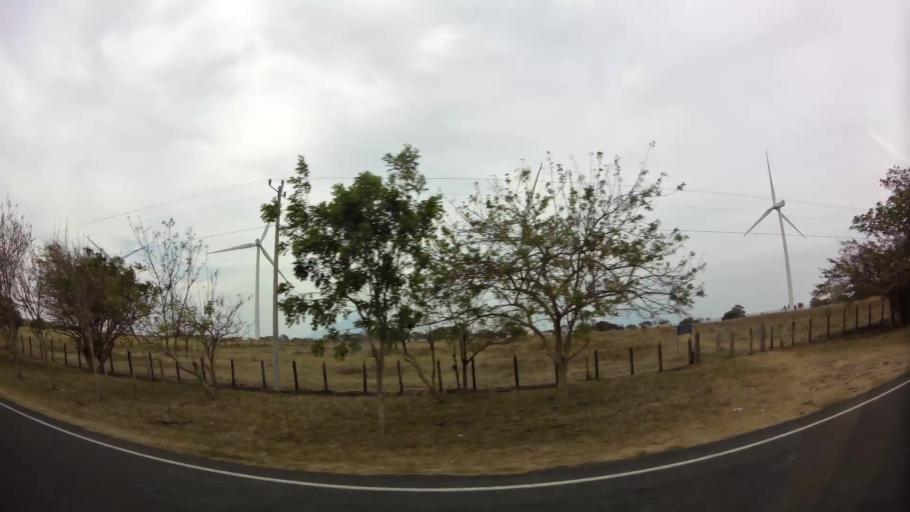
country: NI
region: Rivas
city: Rivas
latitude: 11.3607
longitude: -85.7472
